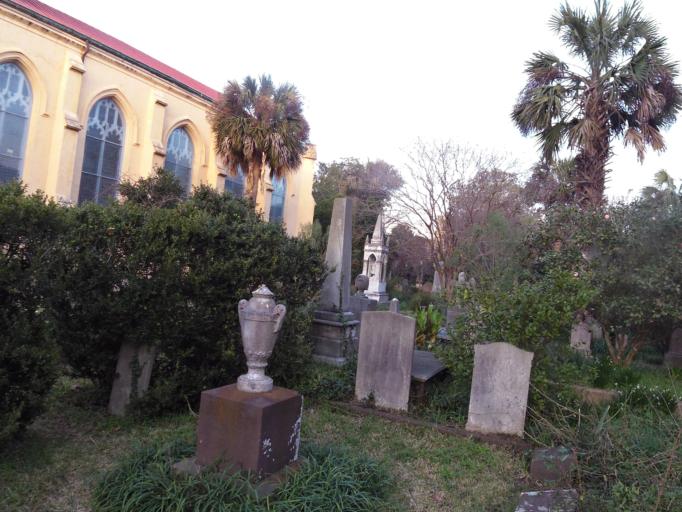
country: US
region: South Carolina
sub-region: Charleston County
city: Charleston
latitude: 32.7783
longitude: -79.9346
